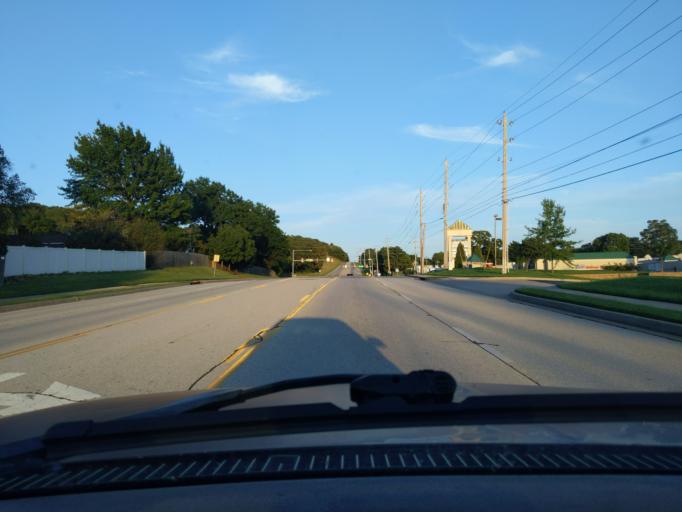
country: US
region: Oklahoma
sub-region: Tulsa County
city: Jenks
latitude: 36.0464
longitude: -95.9419
